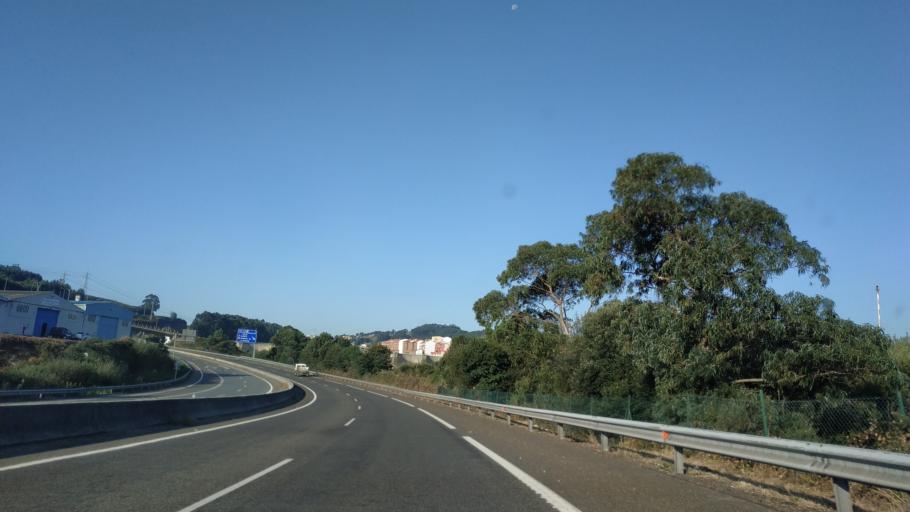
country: ES
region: Galicia
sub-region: Provincia da Coruna
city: A Coruna
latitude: 43.3426
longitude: -8.4469
